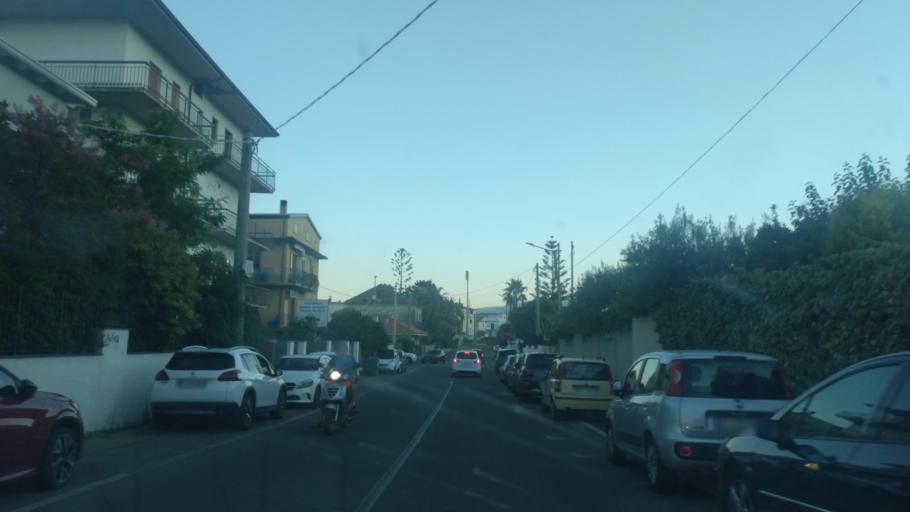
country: IT
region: Calabria
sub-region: Provincia di Catanzaro
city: Montepaone Lido
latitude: 38.7323
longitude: 16.5445
